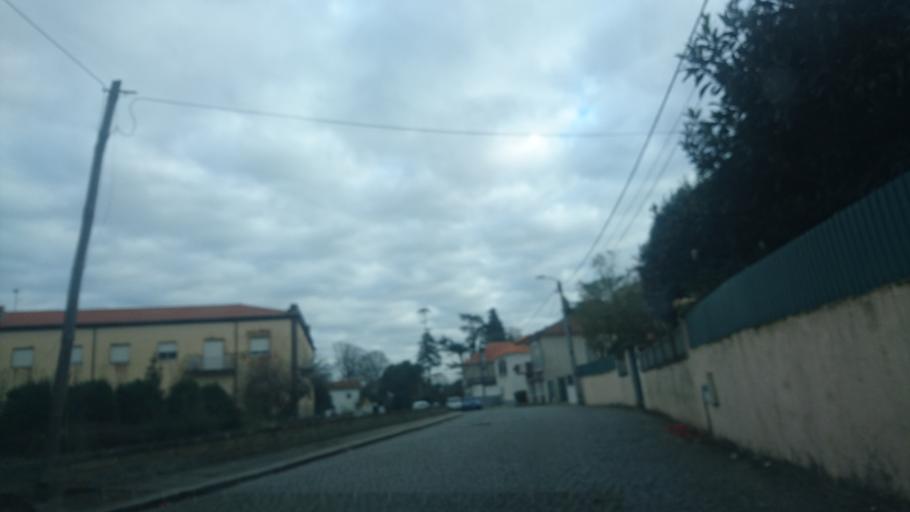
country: PT
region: Aveiro
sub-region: Santa Maria da Feira
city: Pacos de Brandao
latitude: 40.9728
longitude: -8.5858
